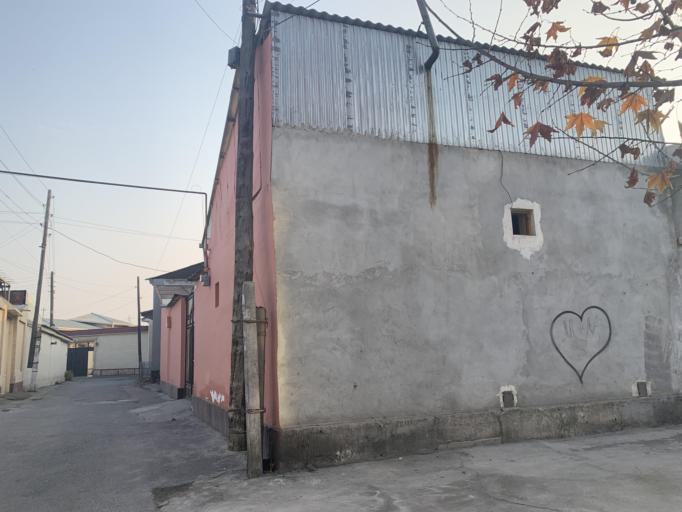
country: UZ
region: Fergana
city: Qo`qon
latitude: 40.5382
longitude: 70.9297
